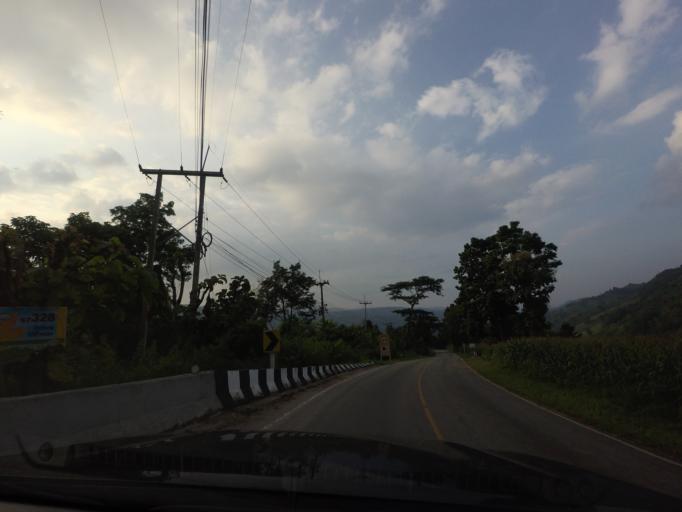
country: TH
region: Loei
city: Na Haeo
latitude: 17.3639
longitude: 101.0499
